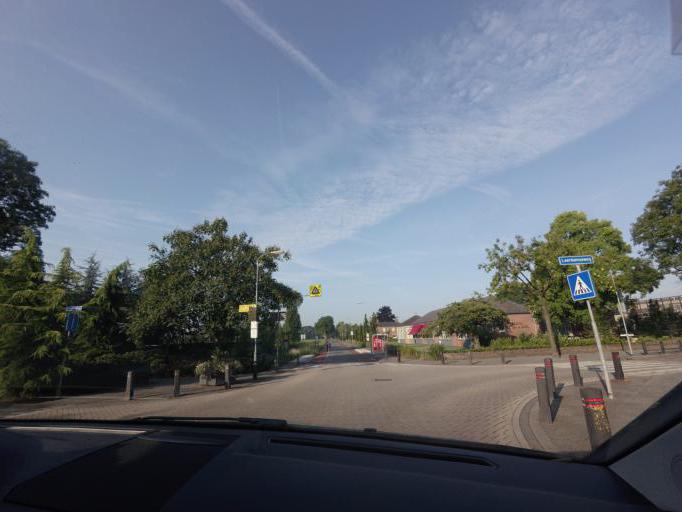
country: NL
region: South Holland
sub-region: Gemeente Leerdam
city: Leerdam
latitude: 51.8808
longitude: 5.1105
